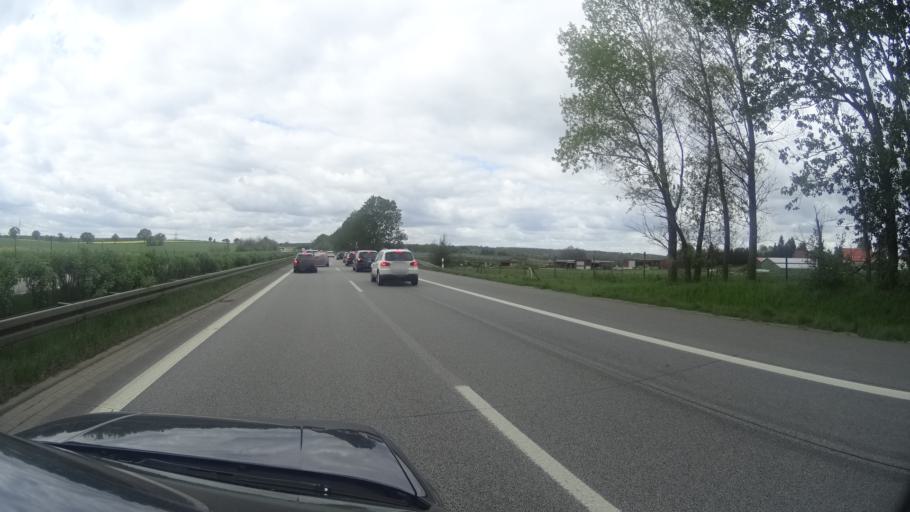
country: DE
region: Mecklenburg-Vorpommern
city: Malchow
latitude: 53.4311
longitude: 12.4192
